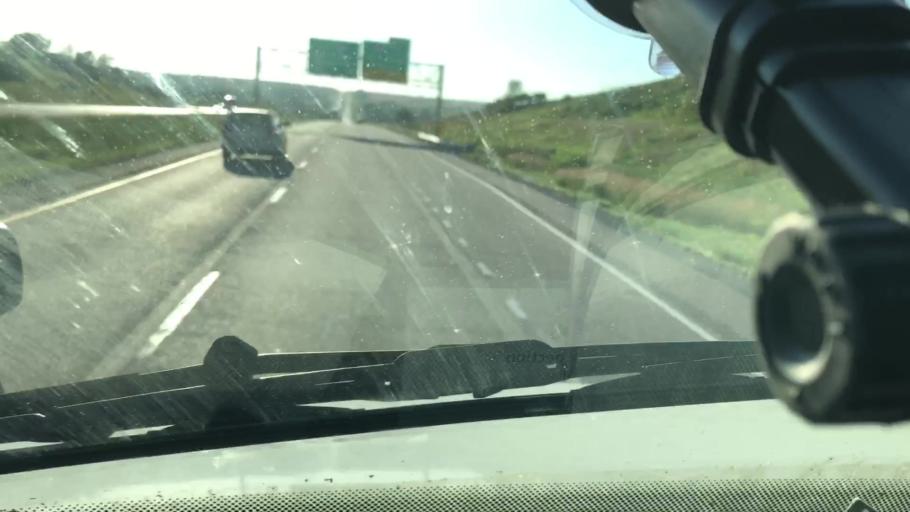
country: US
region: Iowa
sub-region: Pottawattamie County
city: Avoca
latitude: 41.4991
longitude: -95.5739
